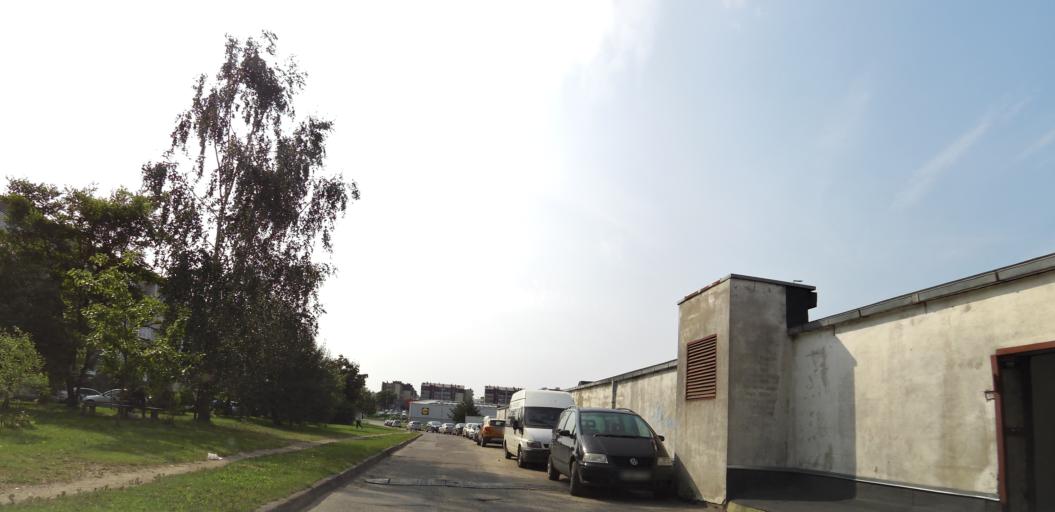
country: LT
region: Vilnius County
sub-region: Vilnius
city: Fabijoniskes
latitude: 54.7392
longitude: 25.2341
